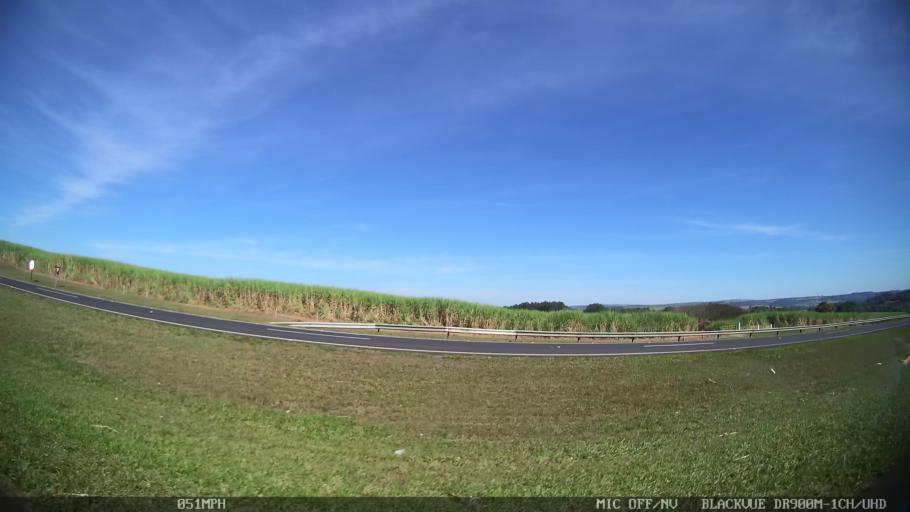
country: BR
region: Sao Paulo
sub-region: Porto Ferreira
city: Porto Ferreira
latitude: -21.7975
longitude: -47.5108
